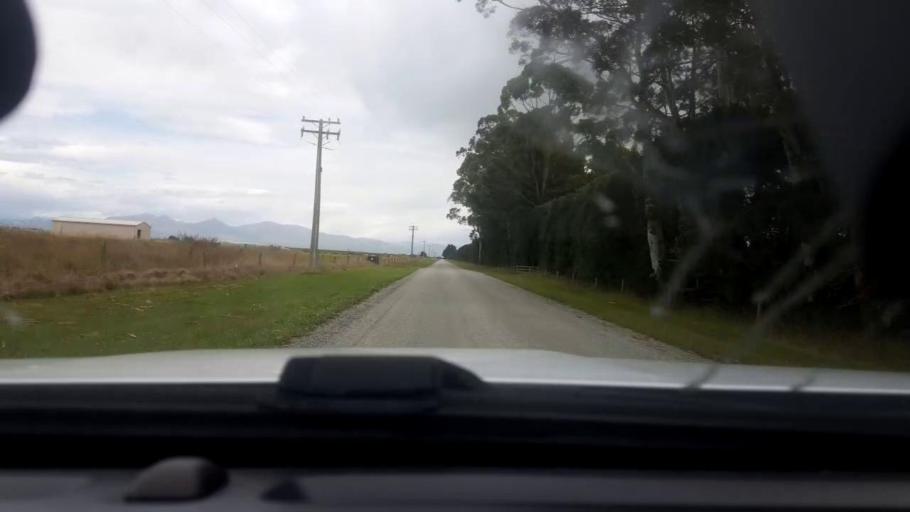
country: NZ
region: Canterbury
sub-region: Timaru District
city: Pleasant Point
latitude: -44.1501
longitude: 171.3936
